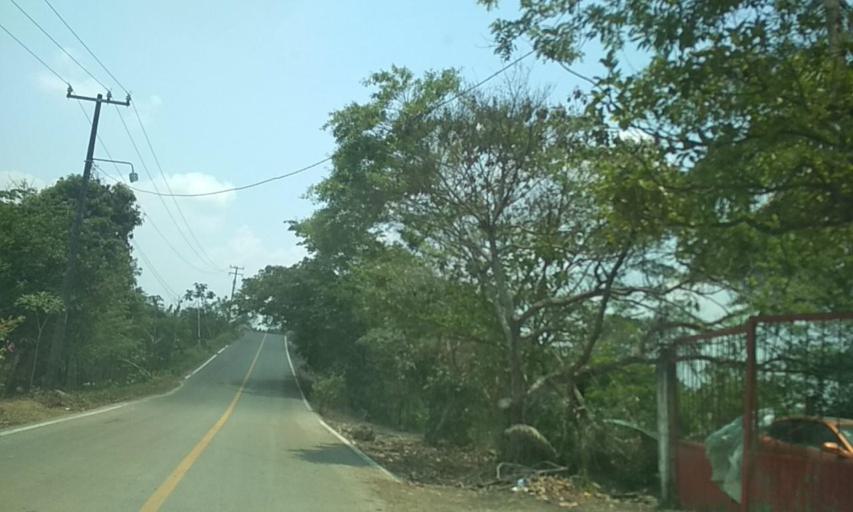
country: MX
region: Tabasco
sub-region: Huimanguillo
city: Francisco Rueda
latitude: 17.7574
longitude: -94.0026
